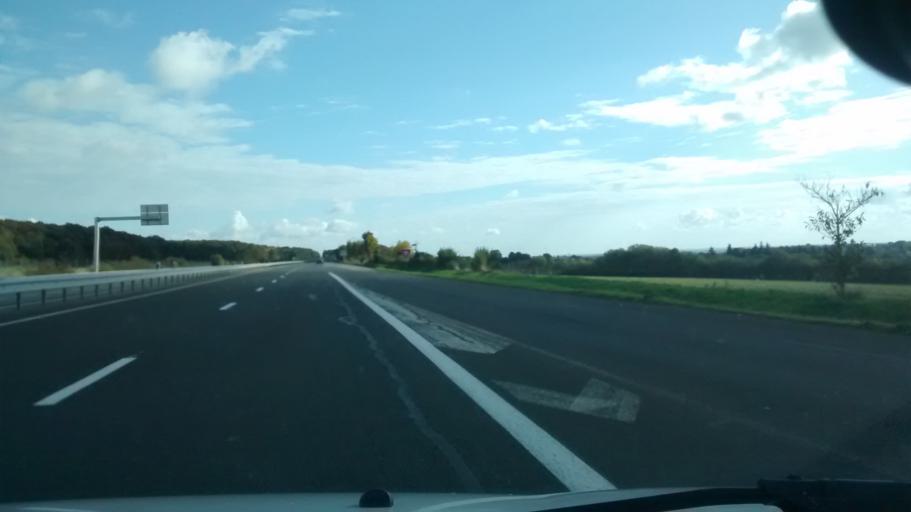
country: FR
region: Pays de la Loire
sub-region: Departement de Maine-et-Loire
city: Combree
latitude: 47.7179
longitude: -1.0259
